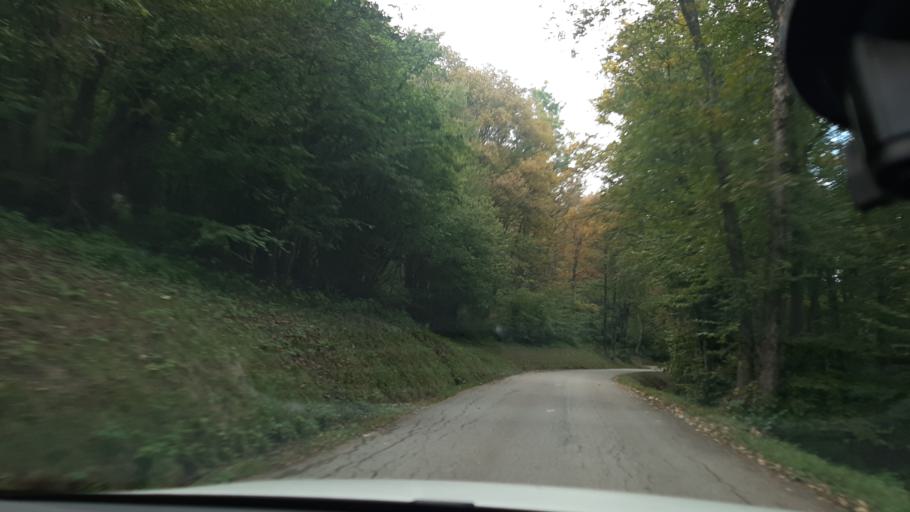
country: FR
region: Rhone-Alpes
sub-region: Departement de la Savoie
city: Villargondran
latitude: 45.2547
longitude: 6.3603
